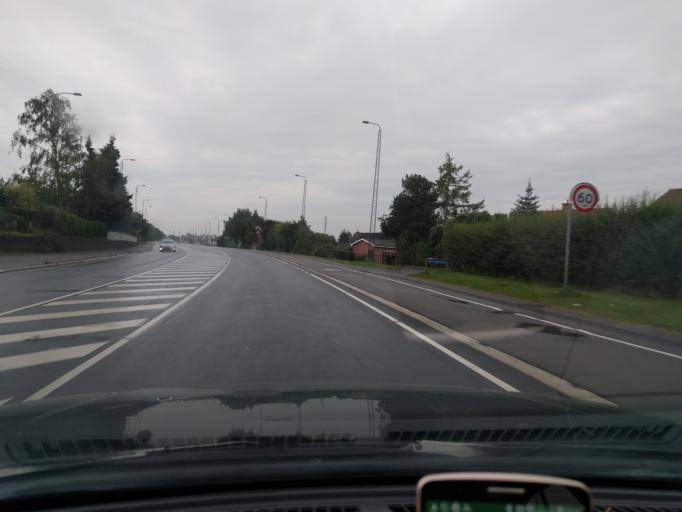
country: DK
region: Zealand
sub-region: Naestved Kommune
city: Naestved
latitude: 55.2038
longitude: 11.7558
